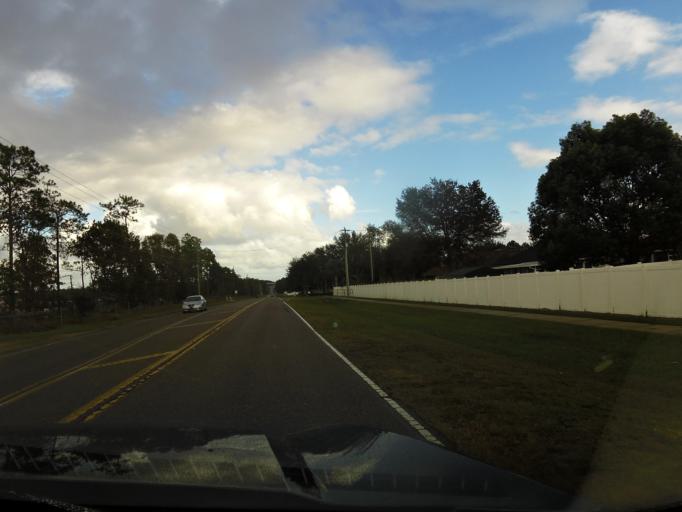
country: US
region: Florida
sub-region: Clay County
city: Asbury Lake
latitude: 30.0462
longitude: -81.7932
